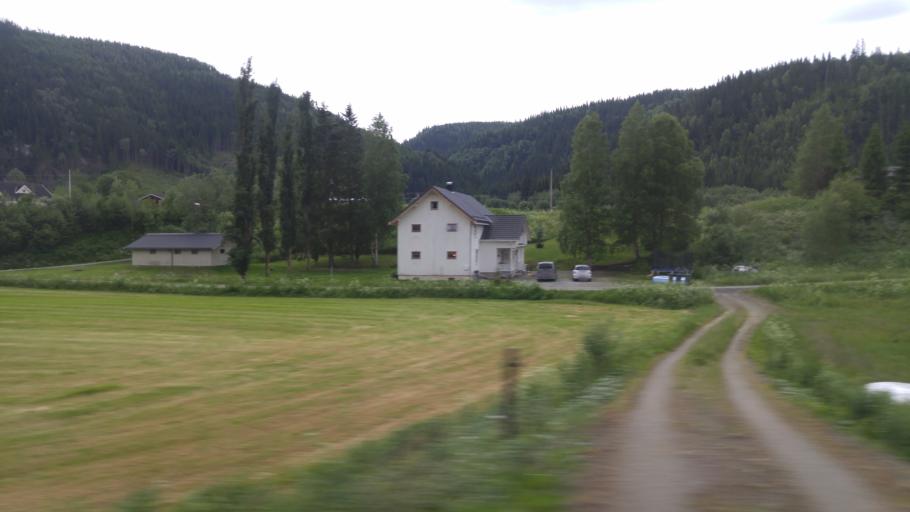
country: NO
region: Nord-Trondelag
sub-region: Levanger
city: Skogn
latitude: 63.4575
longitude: 11.3447
